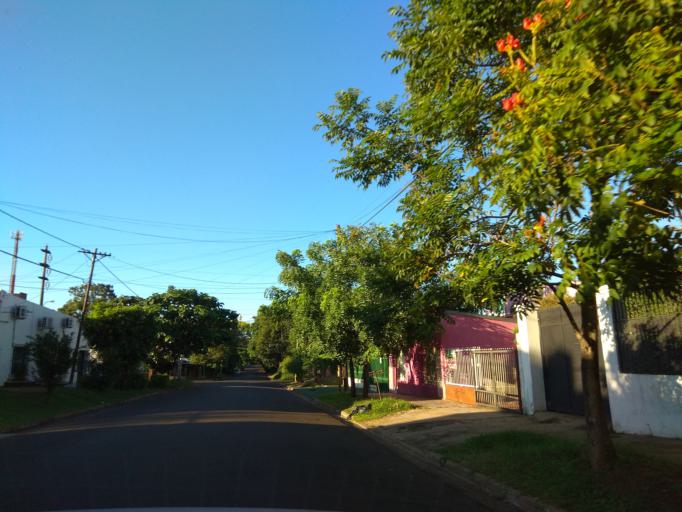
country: AR
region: Misiones
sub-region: Departamento de Capital
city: Posadas
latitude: -27.3755
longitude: -55.9121
